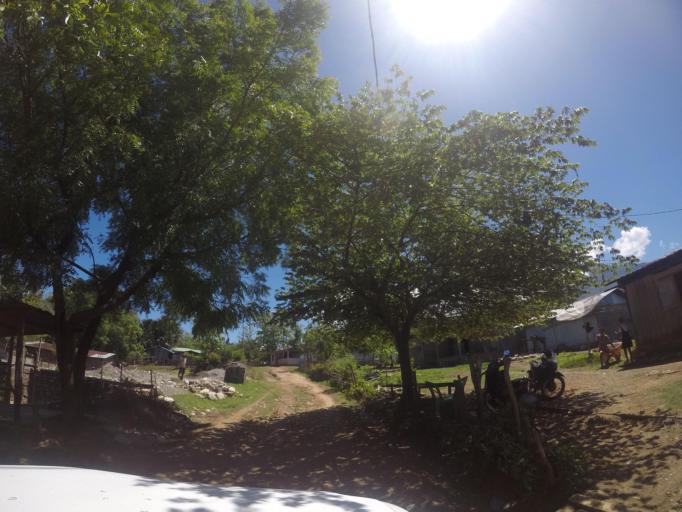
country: TL
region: Bobonaro
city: Maliana
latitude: -8.9665
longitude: 125.2099
